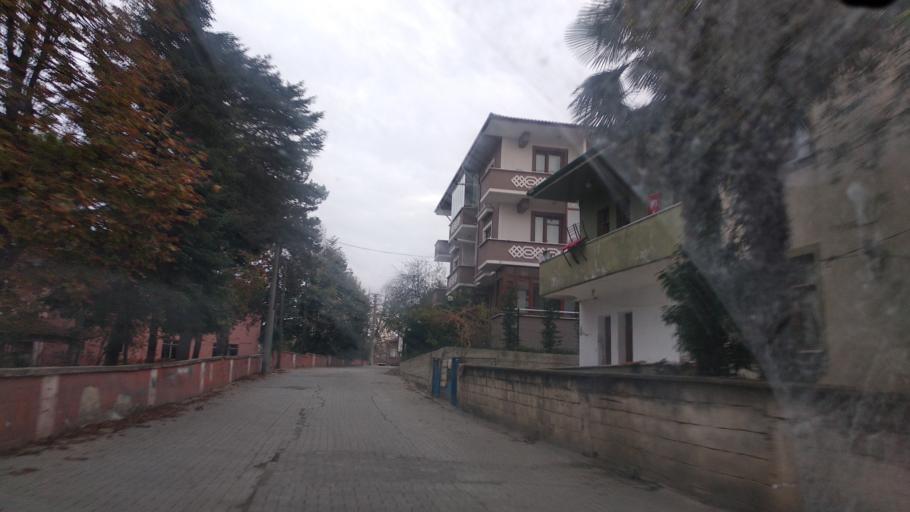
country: TR
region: Sakarya
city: Karasu
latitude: 41.0912
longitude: 30.6984
